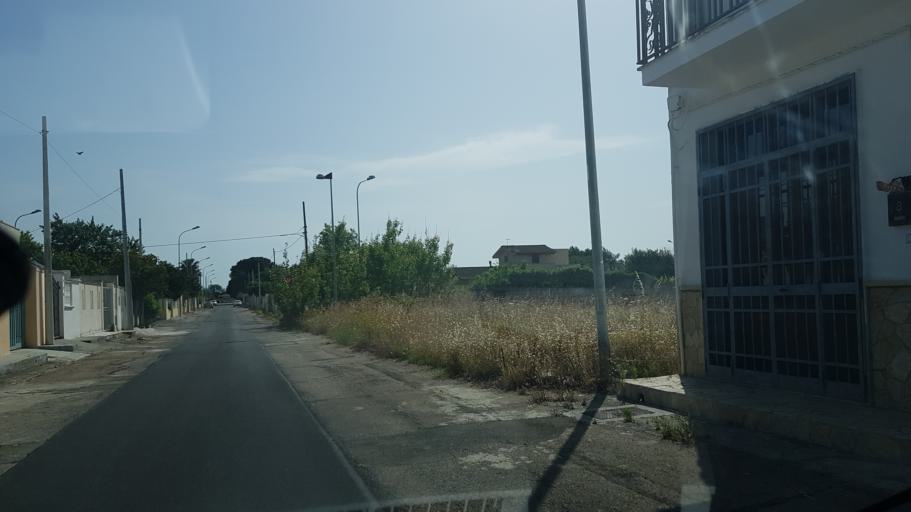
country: IT
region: Apulia
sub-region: Provincia di Brindisi
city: Torchiarolo
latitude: 40.5310
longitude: 18.0760
